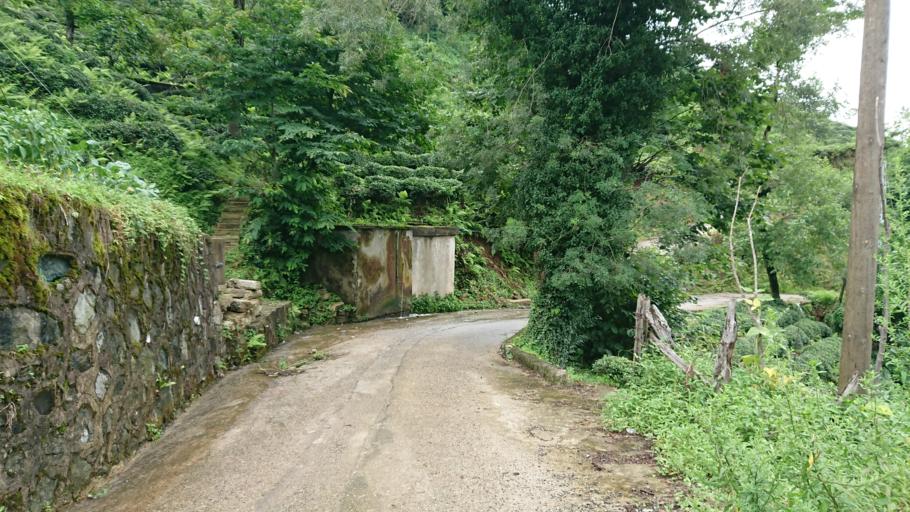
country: TR
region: Rize
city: Rize
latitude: 40.9748
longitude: 40.4854
